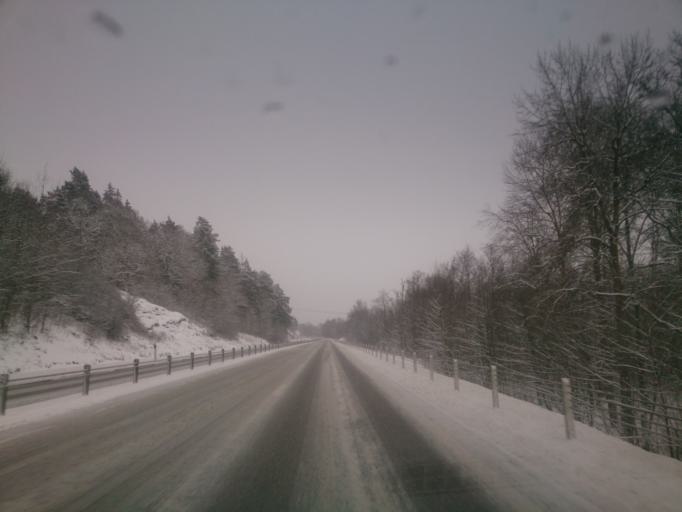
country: SE
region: OEstergoetland
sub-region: Finspangs Kommun
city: Finspang
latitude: 58.7033
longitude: 15.8795
